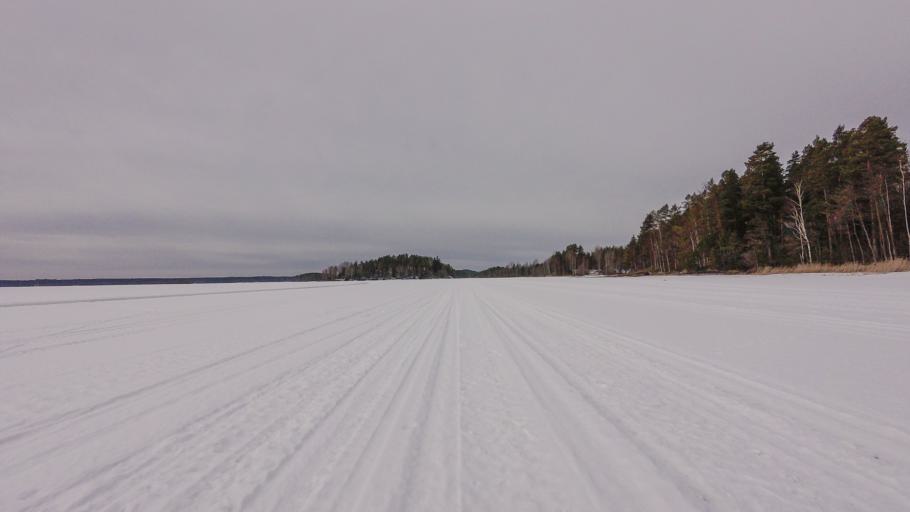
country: FI
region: Southern Savonia
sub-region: Savonlinna
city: Rantasalmi
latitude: 62.1142
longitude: 28.3417
